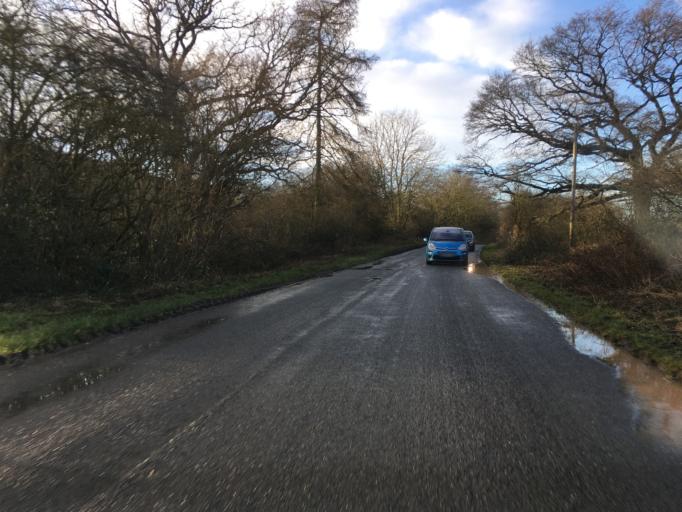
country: GB
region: England
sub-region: Warwickshire
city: Henley in Arden
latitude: 52.2219
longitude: -1.7896
